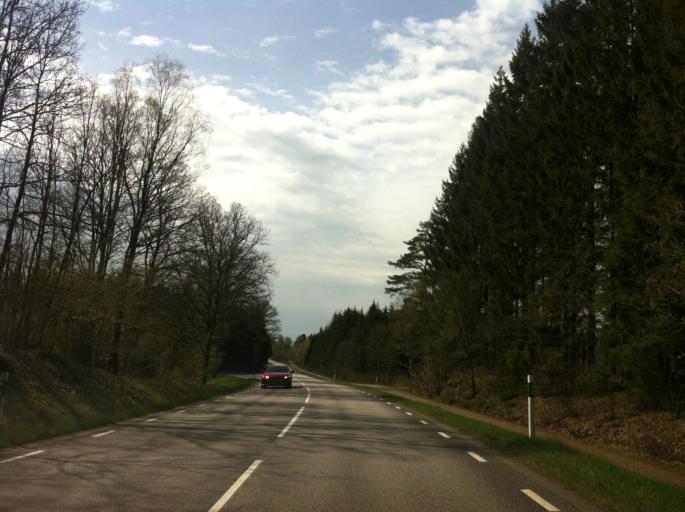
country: SE
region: Vaestra Goetaland
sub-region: Marks Kommun
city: Horred
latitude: 57.1524
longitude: 12.7299
